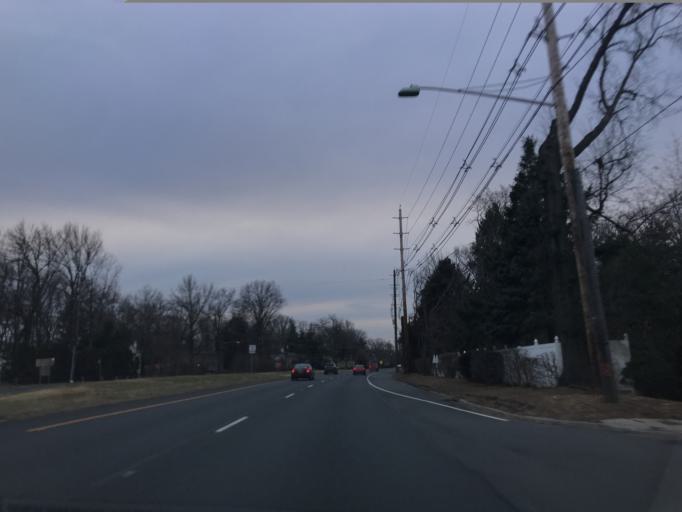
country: US
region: New Jersey
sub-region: Middlesex County
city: Milltown
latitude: 40.4527
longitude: -74.4590
